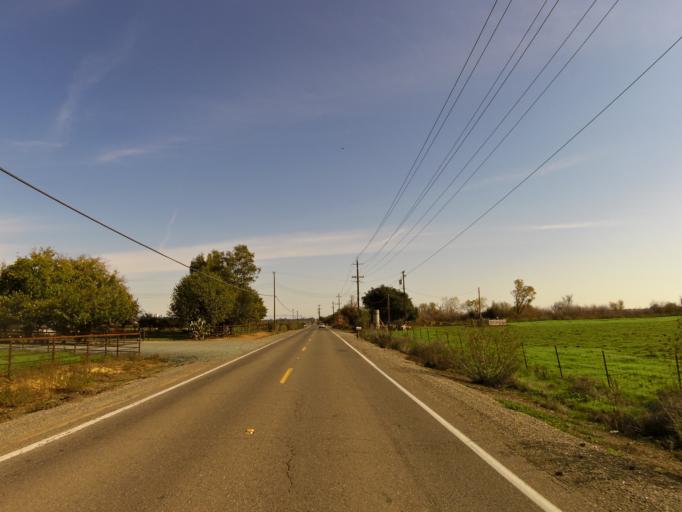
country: US
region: California
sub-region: San Joaquin County
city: Thornton
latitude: 38.2904
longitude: -121.4239
